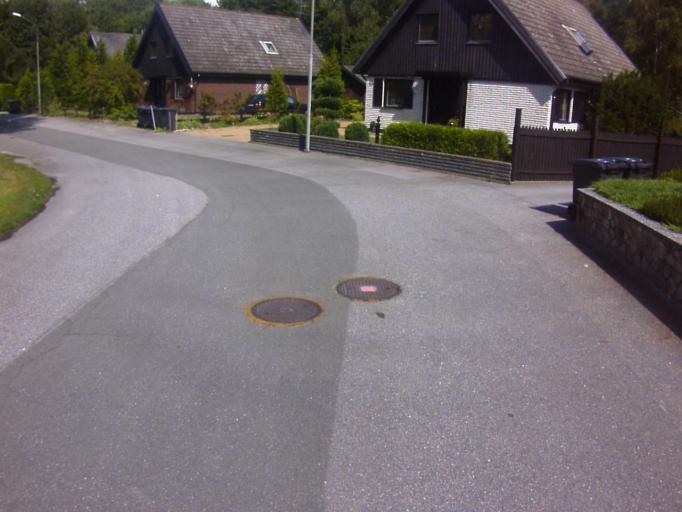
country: SE
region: Blekinge
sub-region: Solvesborgs Kommun
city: Soelvesborg
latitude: 56.0910
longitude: 14.6547
